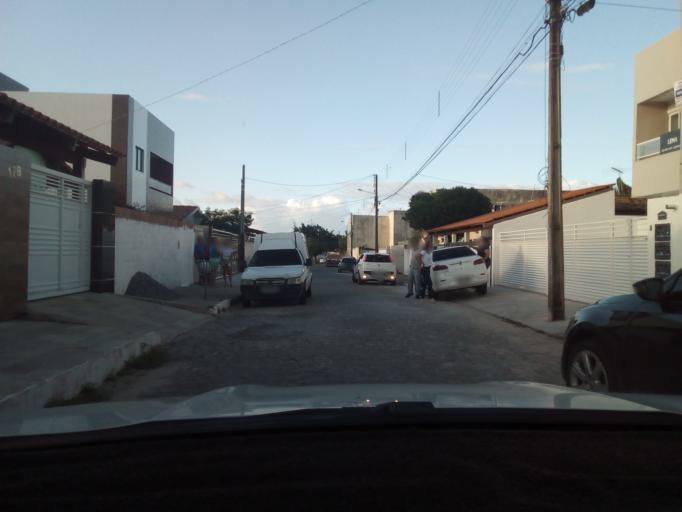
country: BR
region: Paraiba
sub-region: Joao Pessoa
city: Joao Pessoa
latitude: -7.1815
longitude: -34.8377
